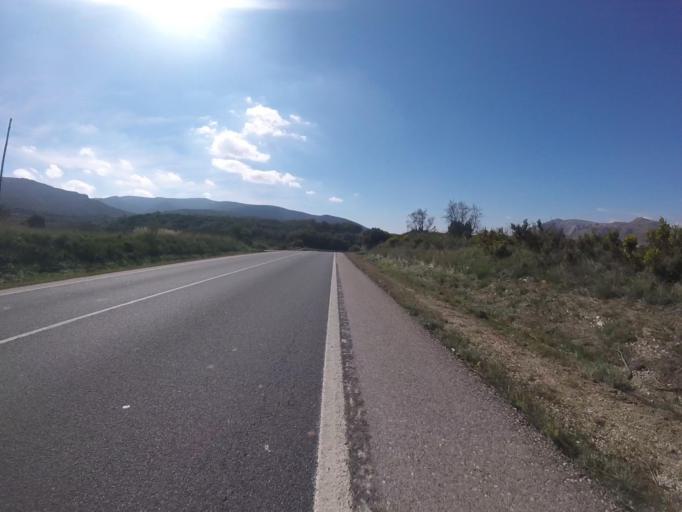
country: ES
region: Valencia
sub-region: Provincia de Castello
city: Sarratella
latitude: 40.3333
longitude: -0.0136
